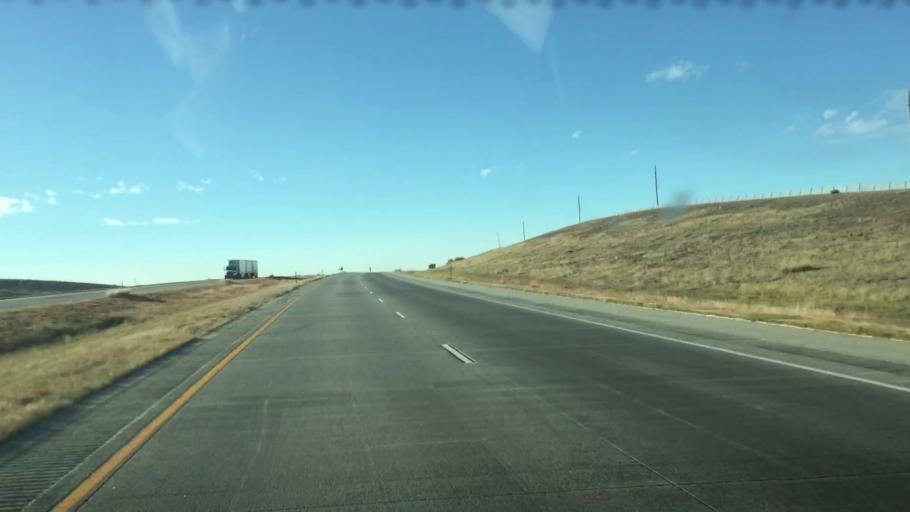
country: US
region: Colorado
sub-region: Lincoln County
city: Limon
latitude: 39.3048
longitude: -103.8178
